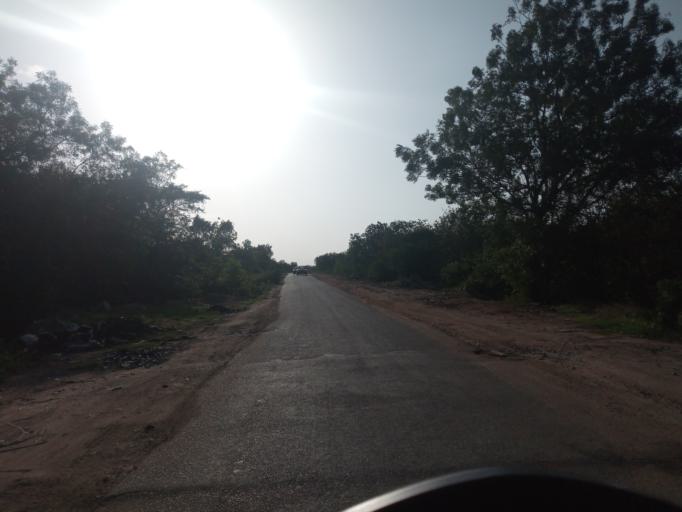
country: IN
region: Telangana
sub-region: Rangareddi
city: Quthbullapur
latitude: 17.5536
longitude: 78.4172
